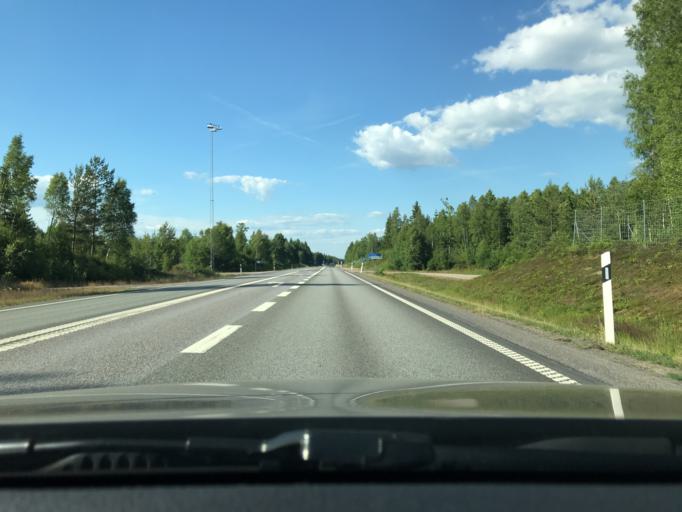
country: SE
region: Kronoberg
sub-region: Almhults Kommun
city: AElmhult
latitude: 56.4723
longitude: 14.1065
